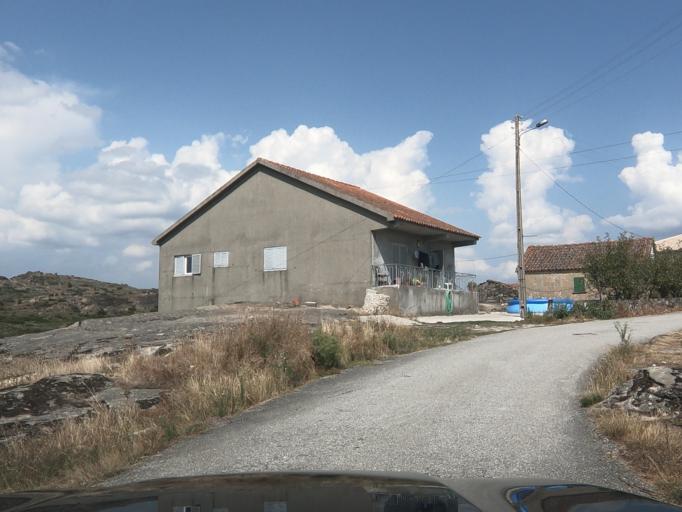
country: PT
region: Vila Real
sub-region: Sabrosa
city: Sabrosa
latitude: 41.3044
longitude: -7.6126
